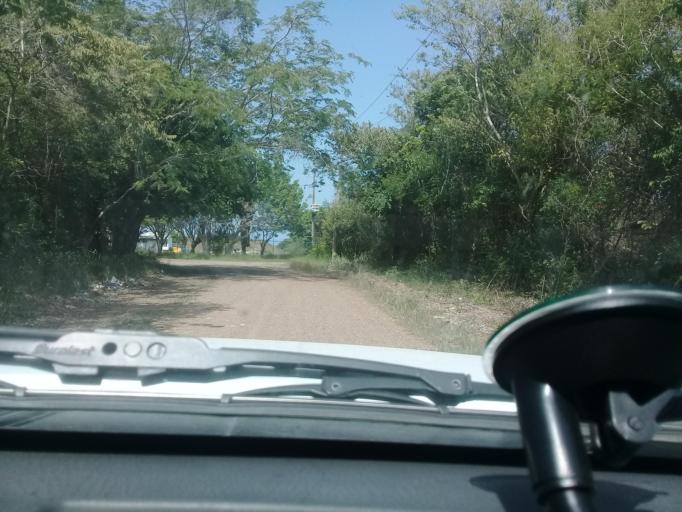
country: MX
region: Veracruz
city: Villa Cuauhtemoc
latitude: 22.1346
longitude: -97.8117
